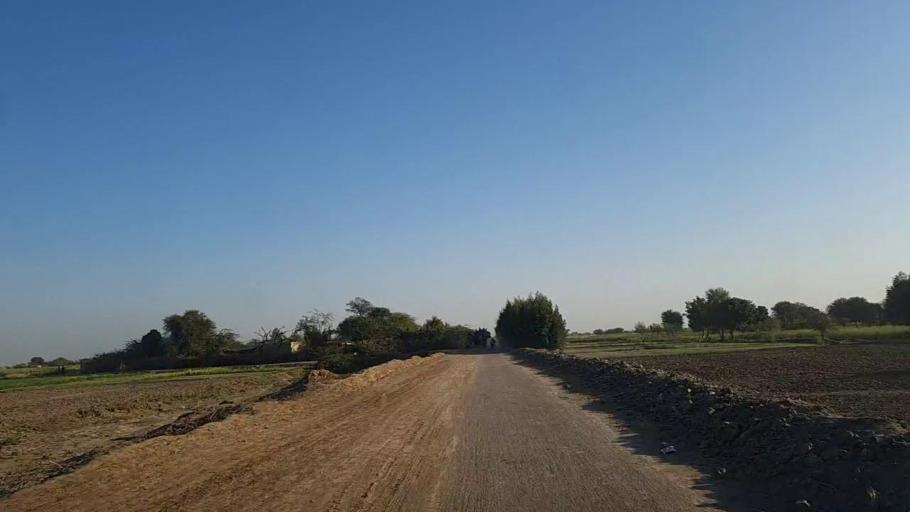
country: PK
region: Sindh
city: Naukot
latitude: 24.9909
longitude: 69.4023
